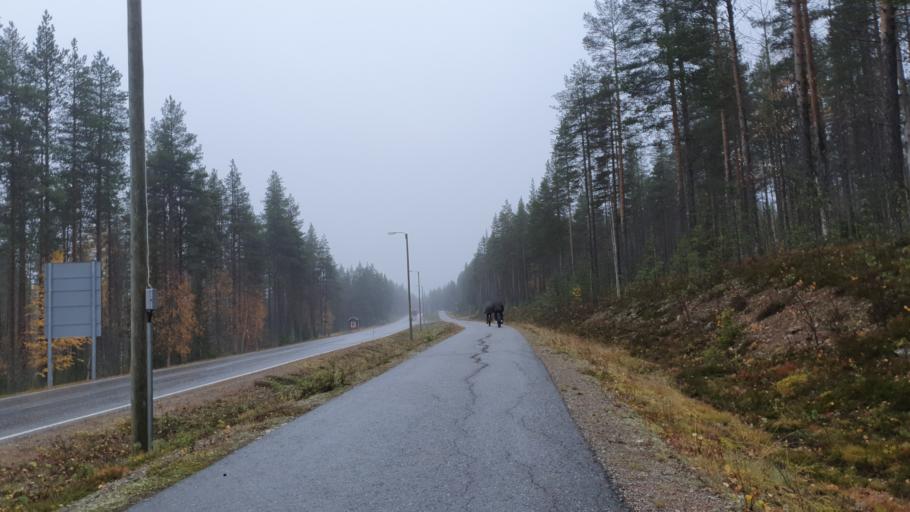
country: FI
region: Lapland
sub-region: Tunturi-Lappi
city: Kolari
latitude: 67.6006
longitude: 24.1253
